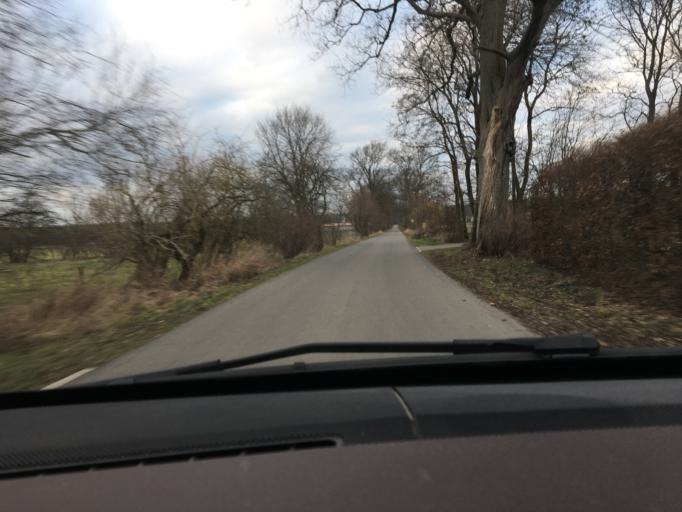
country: DE
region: Brandenburg
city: Marienwerder
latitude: 52.8574
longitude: 13.5059
